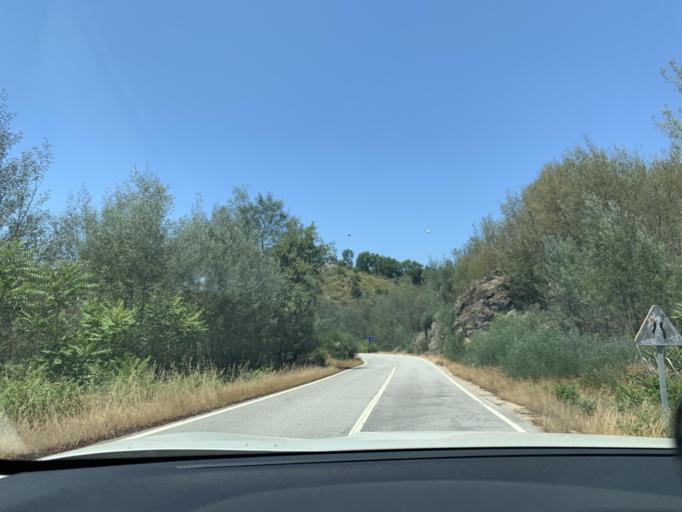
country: PT
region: Guarda
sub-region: Fornos de Algodres
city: Fornos de Algodres
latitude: 40.5688
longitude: -7.5935
